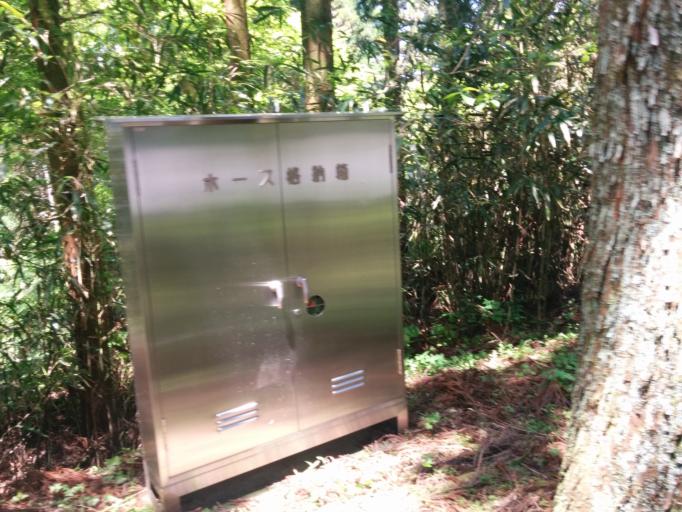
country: JP
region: Shiga Prefecture
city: Otsu-shi
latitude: 35.0744
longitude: 135.8334
